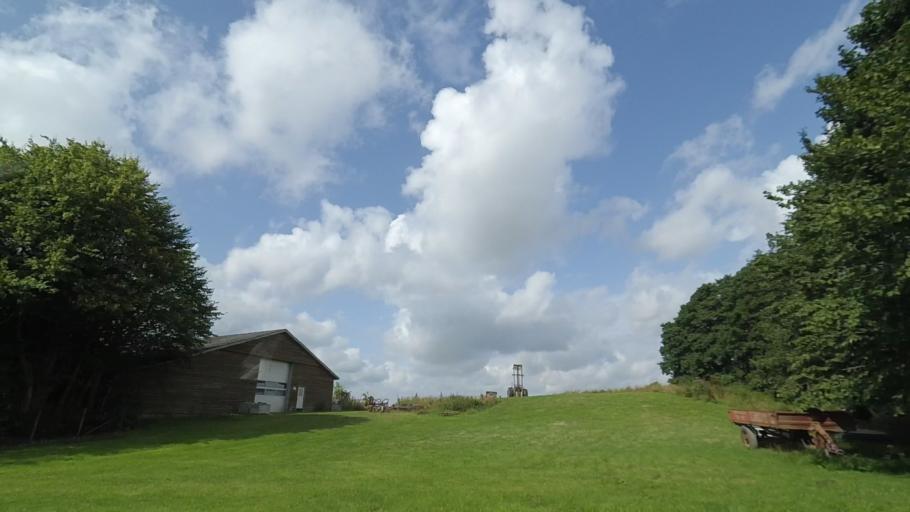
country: DK
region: Central Jutland
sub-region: Syddjurs Kommune
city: Ryomgard
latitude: 56.4786
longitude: 10.5047
